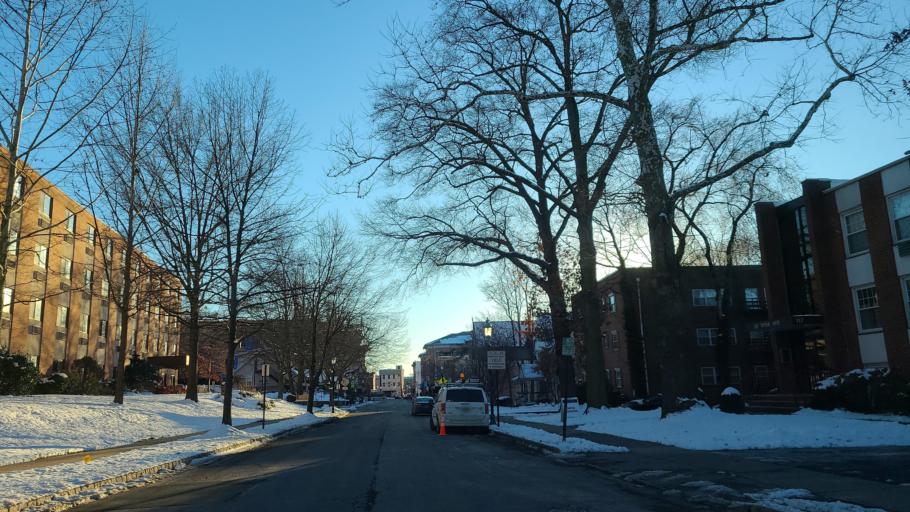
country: US
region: New Jersey
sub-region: Essex County
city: South Orange
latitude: 40.7484
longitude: -74.2574
